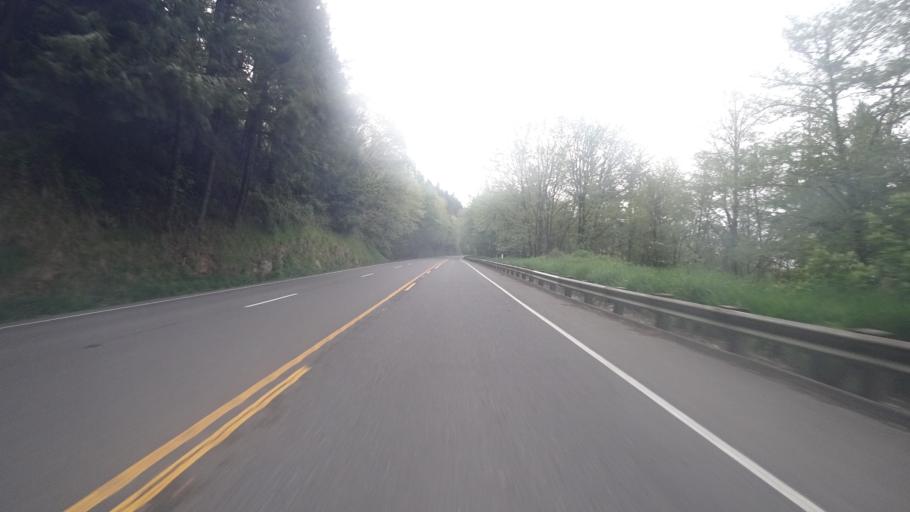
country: US
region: Oregon
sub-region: Douglas County
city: Reedsport
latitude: 43.7501
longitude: -124.1216
